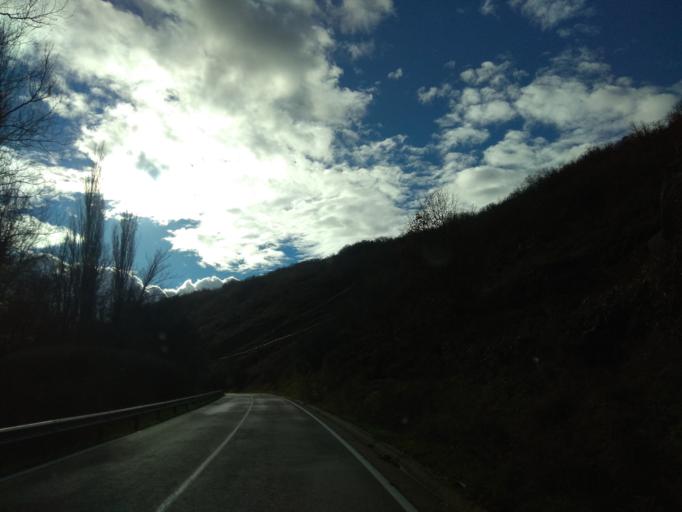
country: ES
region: Cantabria
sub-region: Provincia de Cantabria
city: San Martin de Elines
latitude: 42.8661
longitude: -3.9128
